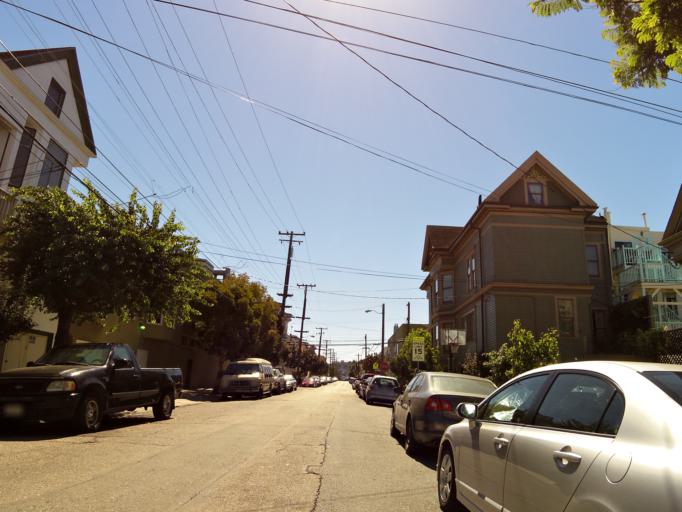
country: US
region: California
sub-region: San Francisco County
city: San Francisco
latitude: 37.7566
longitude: -122.4086
